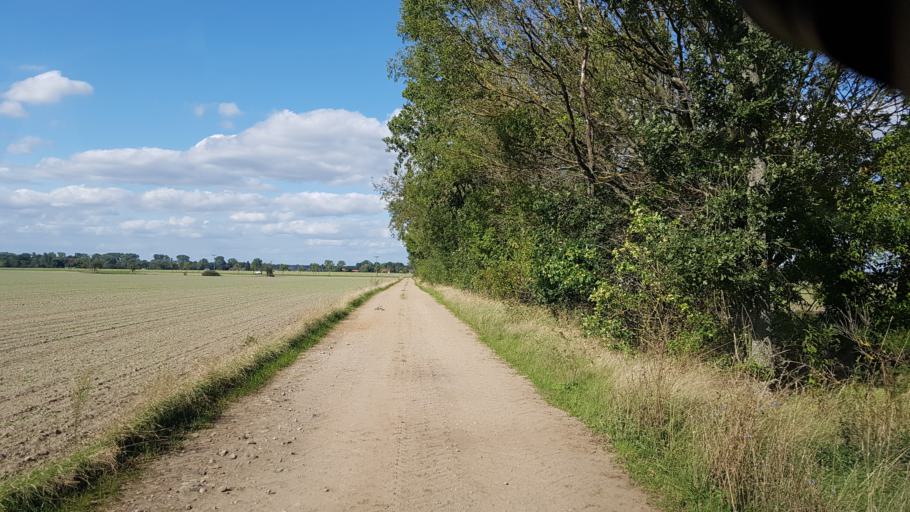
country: DE
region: Brandenburg
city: Sonnewalde
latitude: 51.6911
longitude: 13.6628
